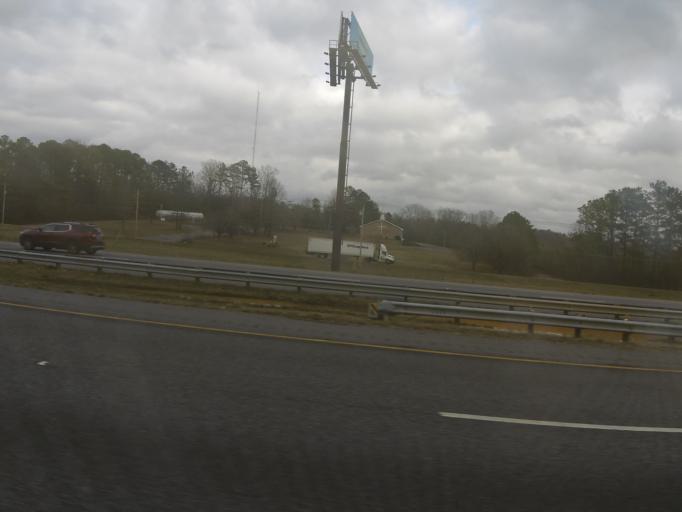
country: US
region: Georgia
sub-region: Gordon County
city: Calhoun
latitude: 34.4896
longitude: -84.9205
